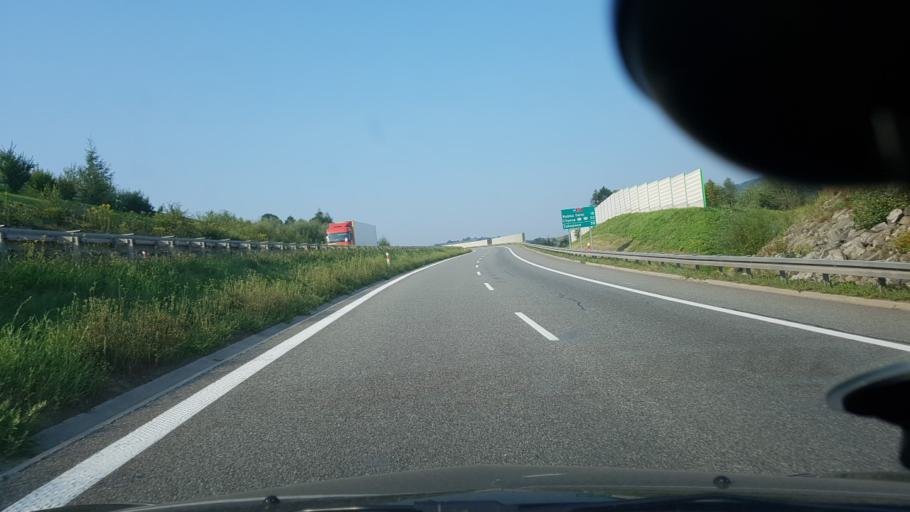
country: PL
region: Lesser Poland Voivodeship
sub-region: Powiat myslenicki
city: Lubien
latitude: 49.7141
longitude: 19.9795
